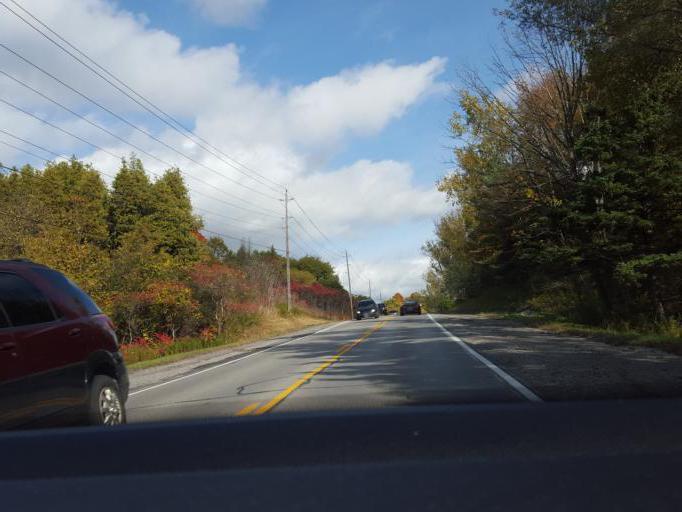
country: CA
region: Ontario
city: Oshawa
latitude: 43.9808
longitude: -78.6722
